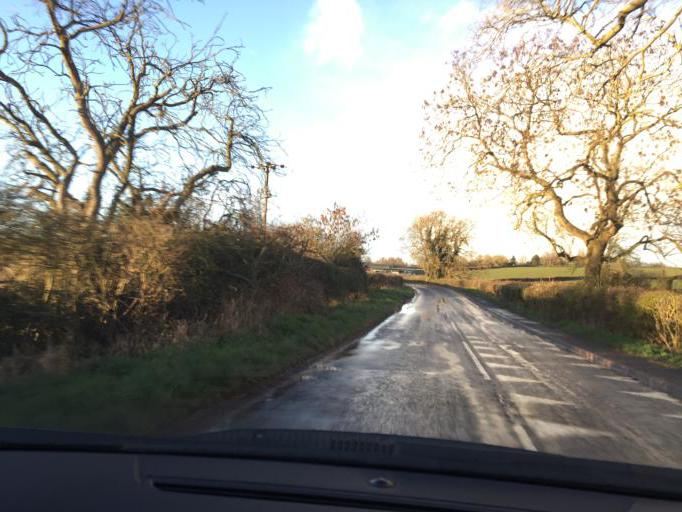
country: GB
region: England
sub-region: Warwickshire
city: Stratford-upon-Avon
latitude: 52.2623
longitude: -1.6944
